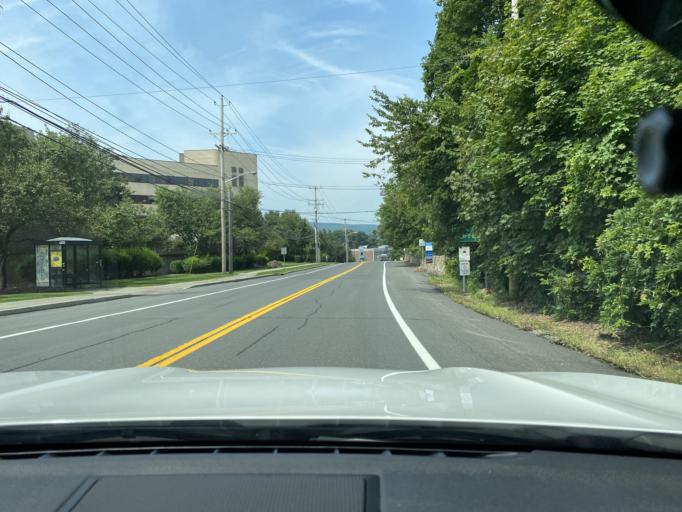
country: US
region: New York
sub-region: Rockland County
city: Suffern
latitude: 41.1123
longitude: -74.1340
